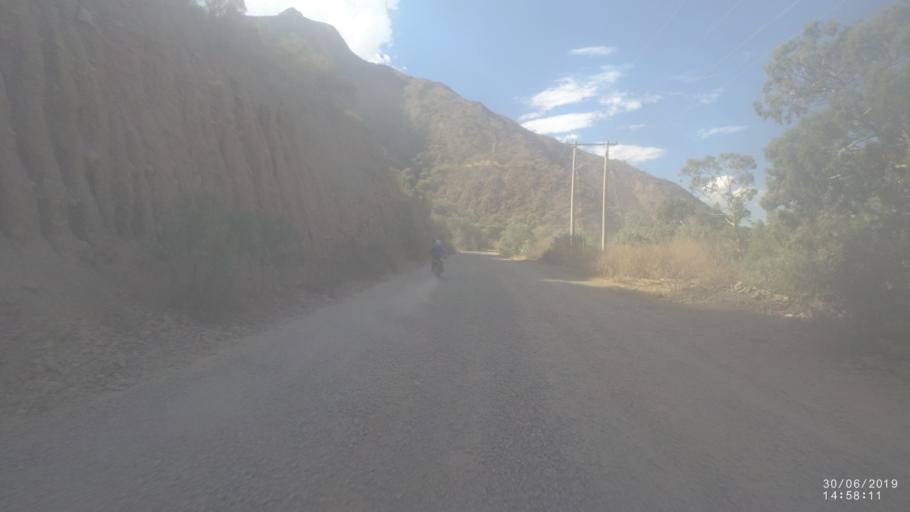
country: BO
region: Cochabamba
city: Irpa Irpa
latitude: -17.7400
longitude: -66.3506
